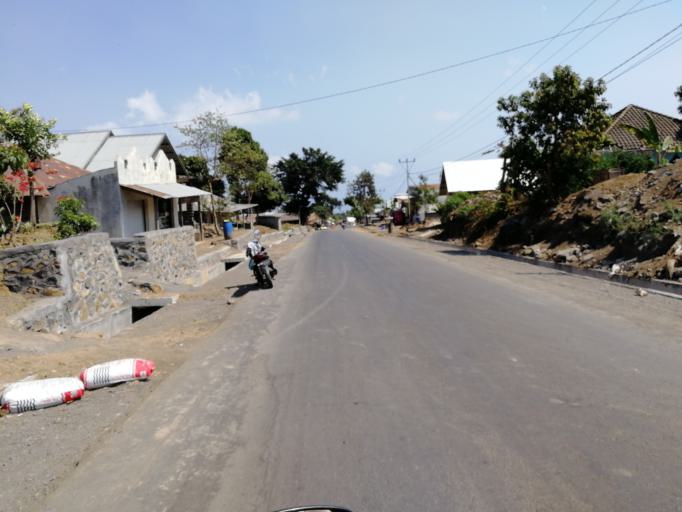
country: ID
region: West Nusa Tenggara
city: Lelongken
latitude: -8.3374
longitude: 116.5000
